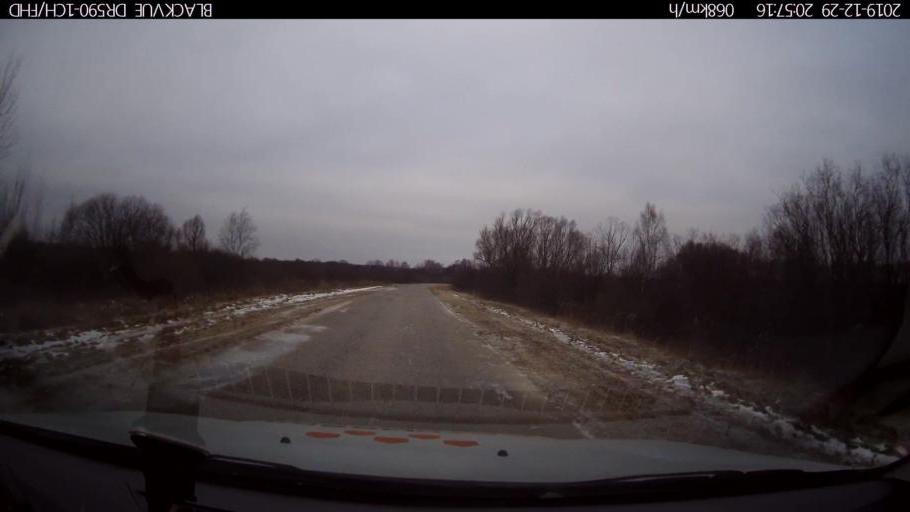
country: RU
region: Nizjnij Novgorod
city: Afonino
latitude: 56.1594
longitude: 43.9926
